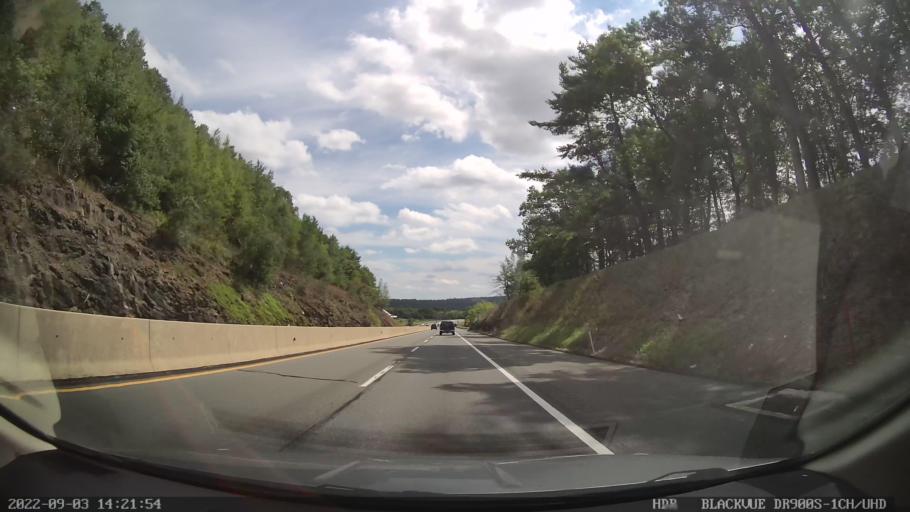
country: US
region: Pennsylvania
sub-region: Carbon County
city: Weissport East
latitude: 40.8647
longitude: -75.6517
